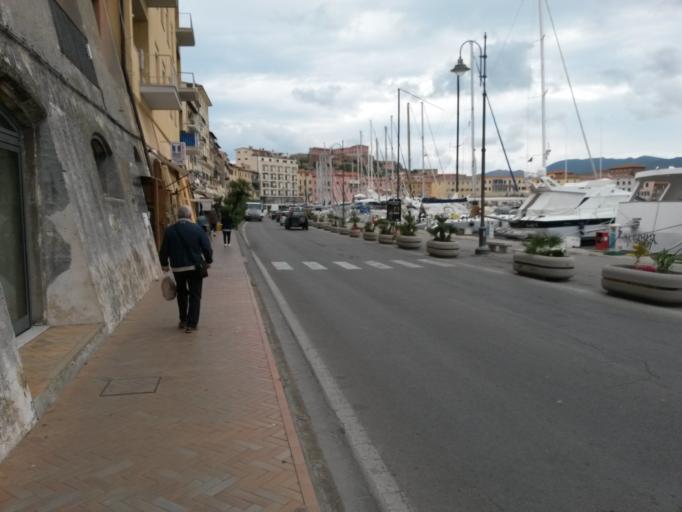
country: IT
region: Tuscany
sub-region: Provincia di Livorno
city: Portoferraio
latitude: 42.8133
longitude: 10.3280
